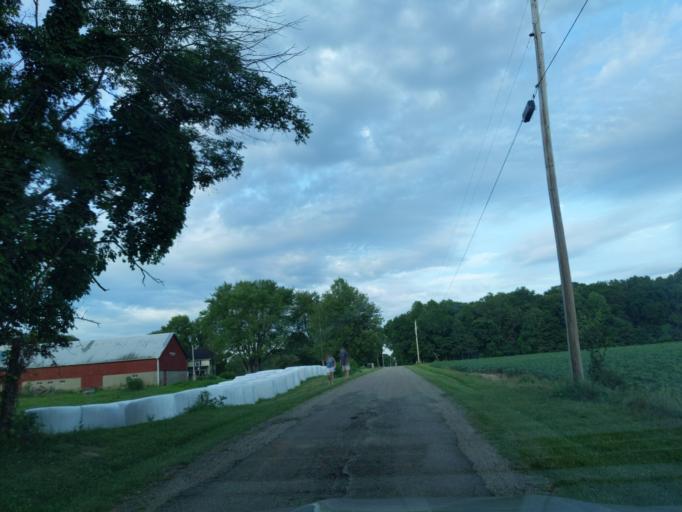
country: US
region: Indiana
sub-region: Ripley County
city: Sunman
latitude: 39.3101
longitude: -85.0927
